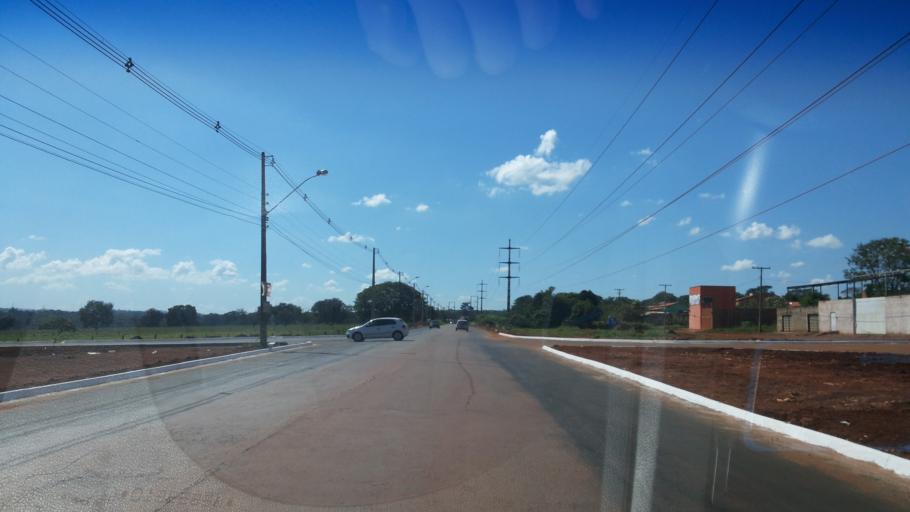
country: BR
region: Goias
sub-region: Goiania
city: Goiania
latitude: -16.5908
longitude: -49.2722
